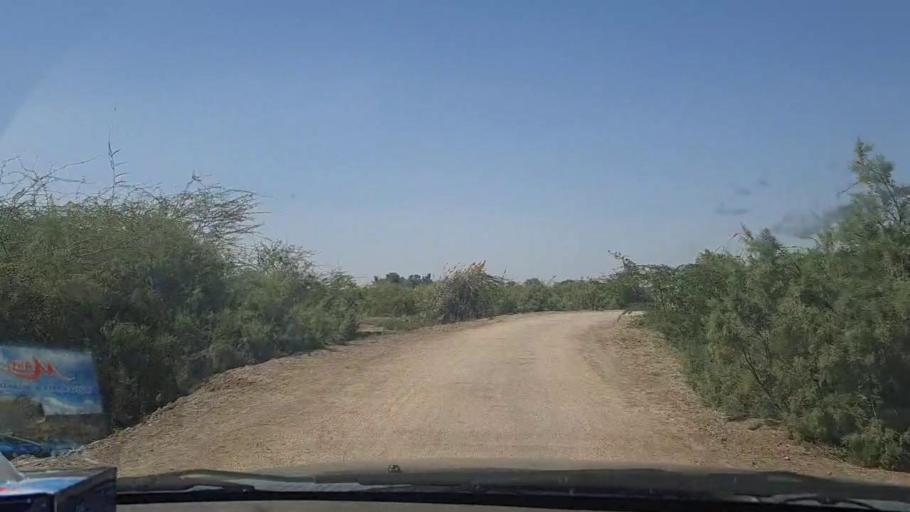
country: PK
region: Sindh
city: Chuhar Jamali
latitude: 24.2829
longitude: 67.7606
